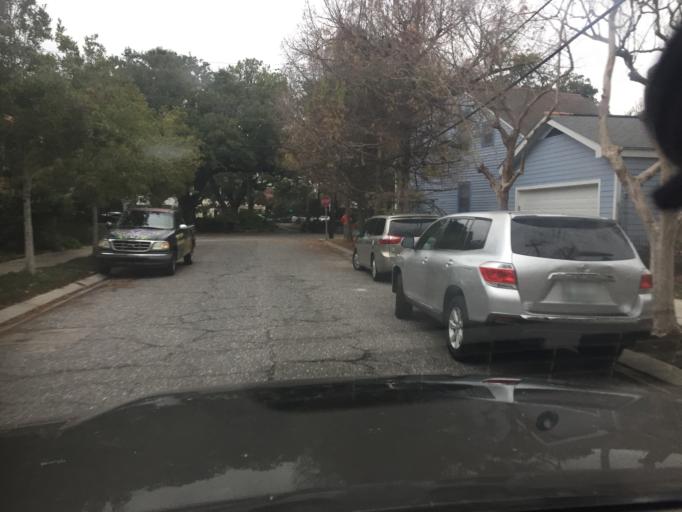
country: US
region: Louisiana
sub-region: Orleans Parish
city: New Orleans
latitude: 29.9795
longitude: -90.0847
